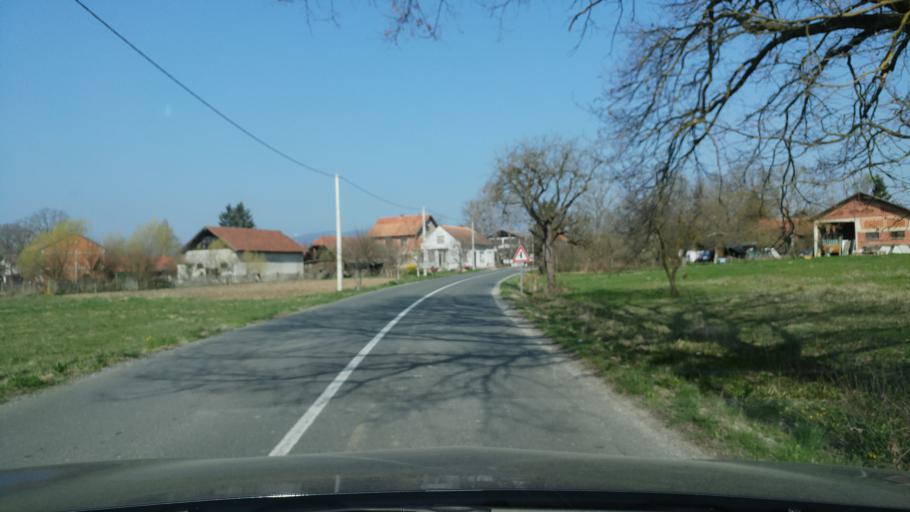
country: HR
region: Zagrebacka
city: Pojatno
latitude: 45.9782
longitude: 15.7326
